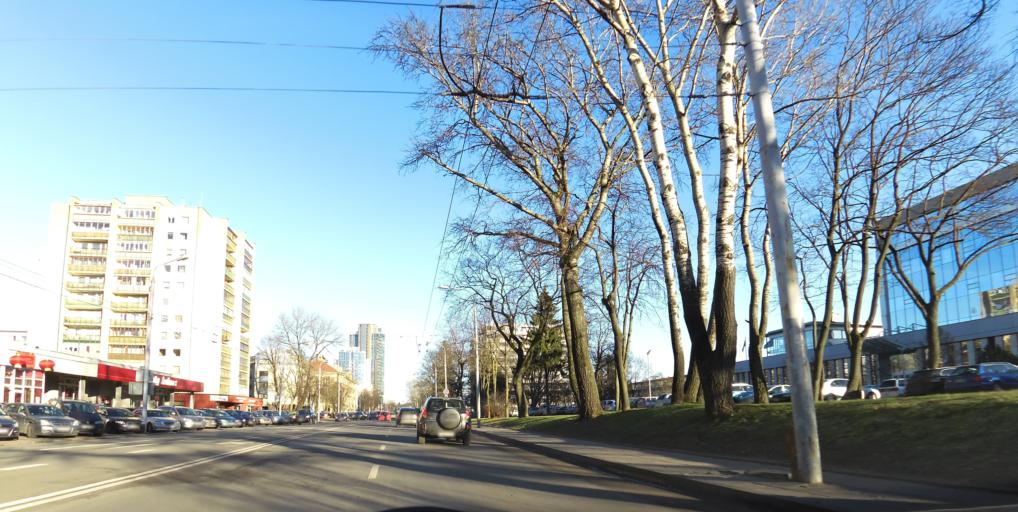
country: LT
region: Vilnius County
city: Vilkpede
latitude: 54.6757
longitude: 25.2518
